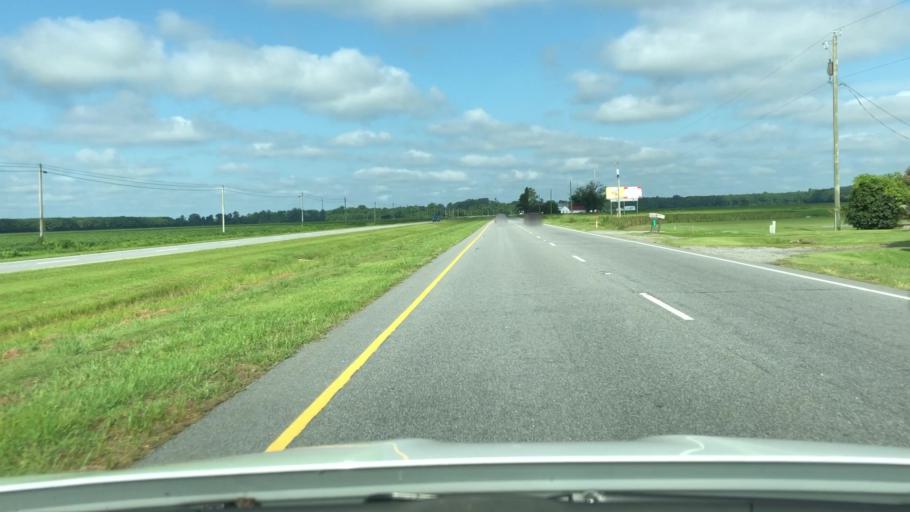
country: US
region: North Carolina
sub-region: Perquimans County
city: Hertford
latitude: 36.2085
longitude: -76.4114
